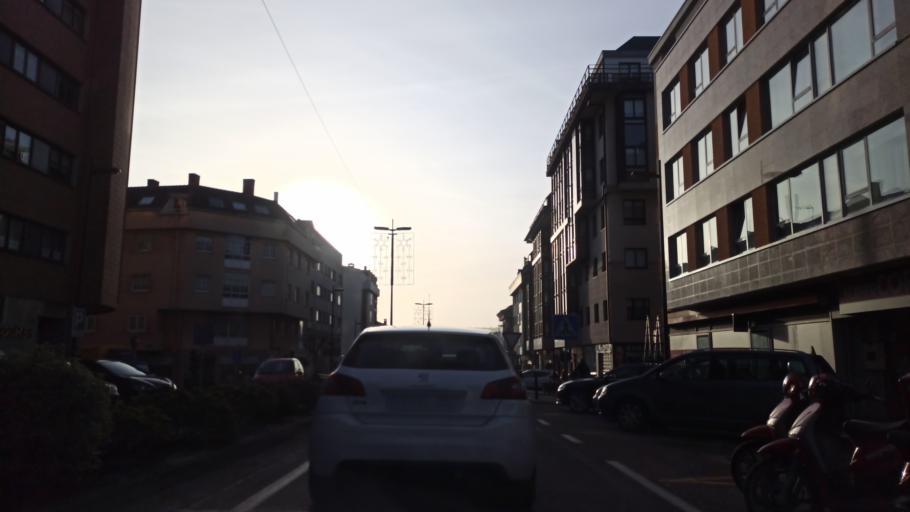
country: ES
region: Galicia
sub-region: Provincia da Coruna
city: Cambre
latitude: 43.3194
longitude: -8.3539
